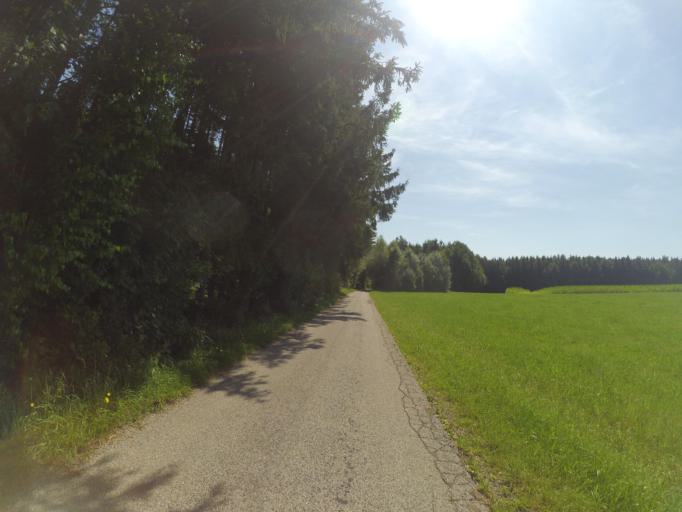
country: DE
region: Bavaria
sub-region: Swabia
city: Baisweil
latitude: 47.9831
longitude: 10.5669
